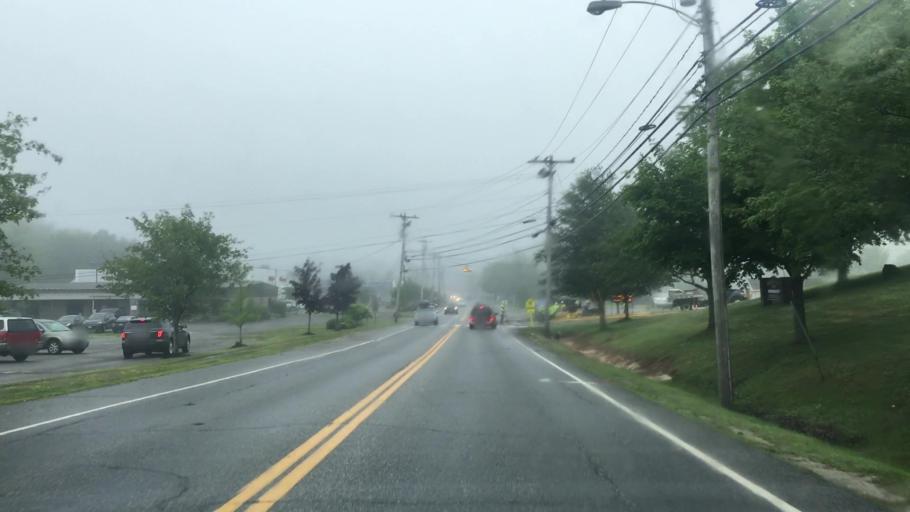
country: US
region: Maine
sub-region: Lincoln County
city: Boothbay Harbor
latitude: 43.8648
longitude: -69.6285
